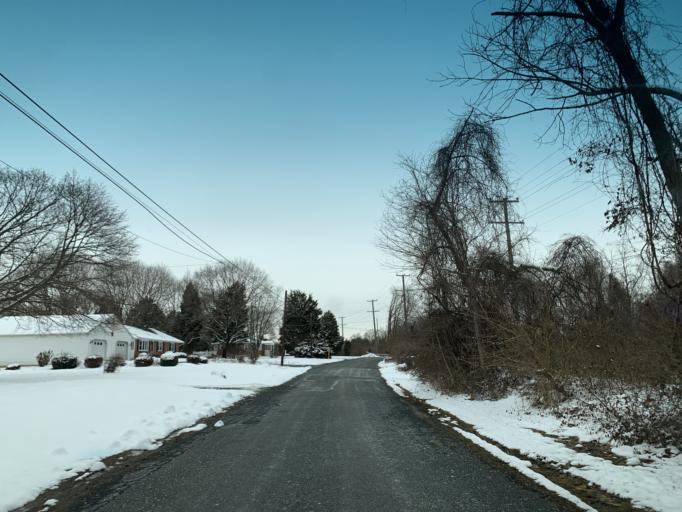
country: US
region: Maryland
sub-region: Harford County
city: Aberdeen
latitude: 39.5748
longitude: -76.1831
